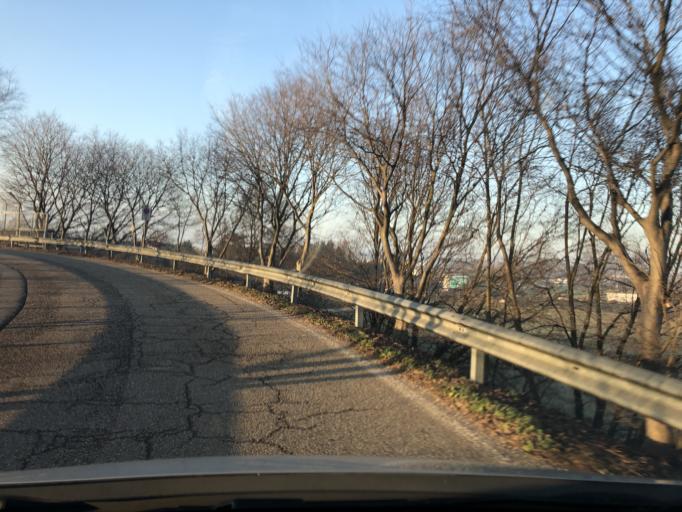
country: IT
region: Veneto
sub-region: Provincia di Verona
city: Caselle
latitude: 45.4142
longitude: 10.8844
